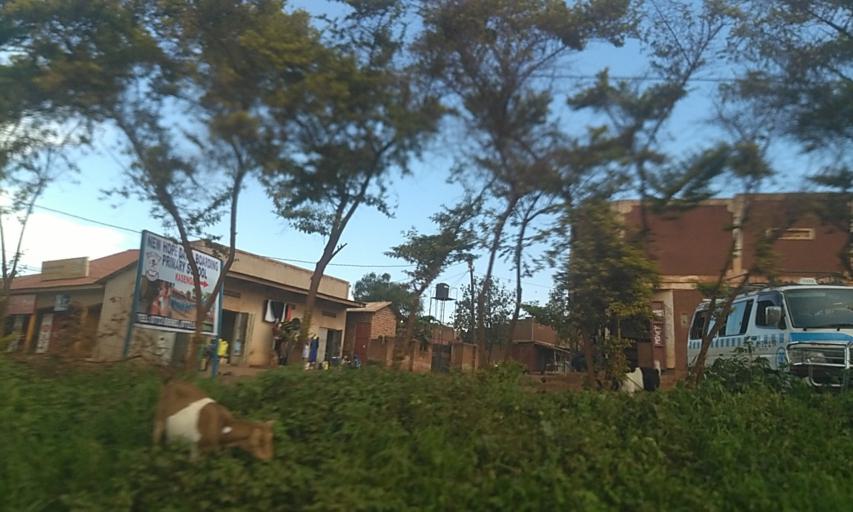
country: UG
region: Central Region
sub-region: Wakiso District
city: Kajansi
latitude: 0.2520
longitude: 32.5048
